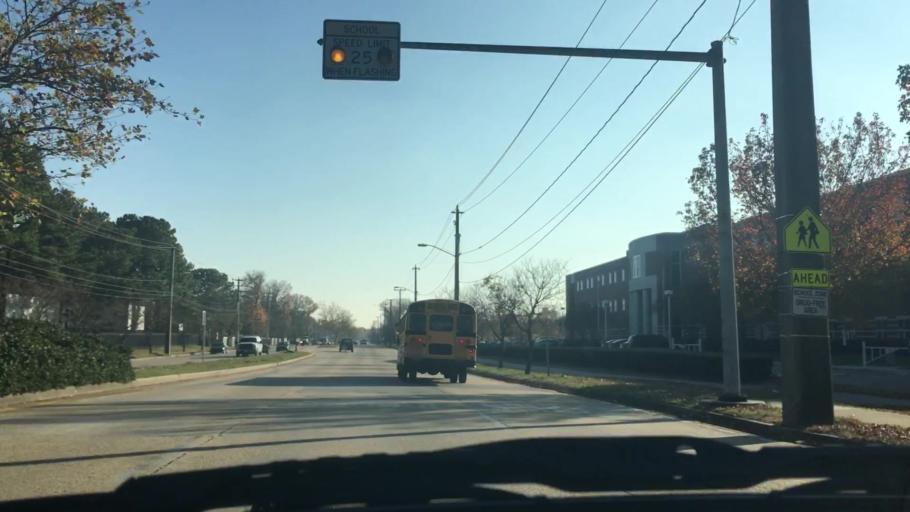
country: US
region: Virginia
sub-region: City of Norfolk
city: Norfolk
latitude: 36.9013
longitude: -76.2394
